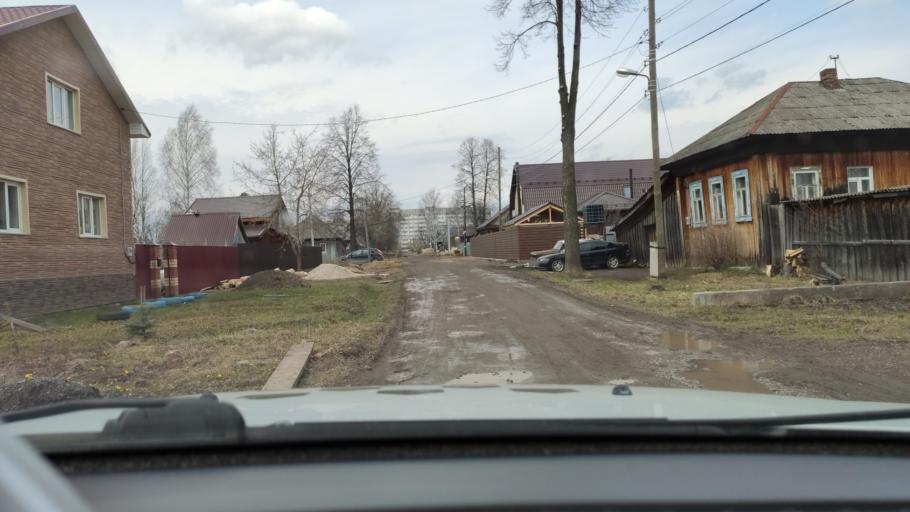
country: RU
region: Perm
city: Perm
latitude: 58.0245
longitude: 56.3317
